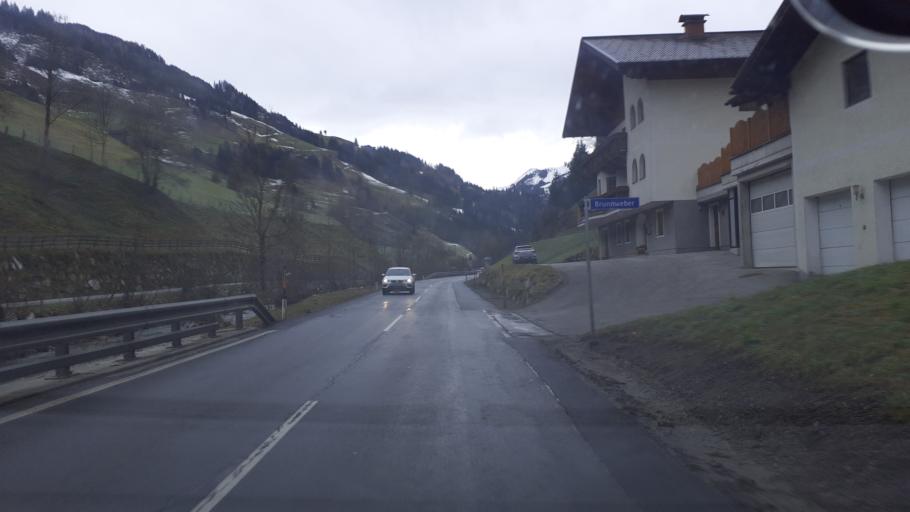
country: AT
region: Salzburg
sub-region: Politischer Bezirk Sankt Johann im Pongau
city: Sankt Johann im Pongau
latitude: 47.2765
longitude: 13.2139
